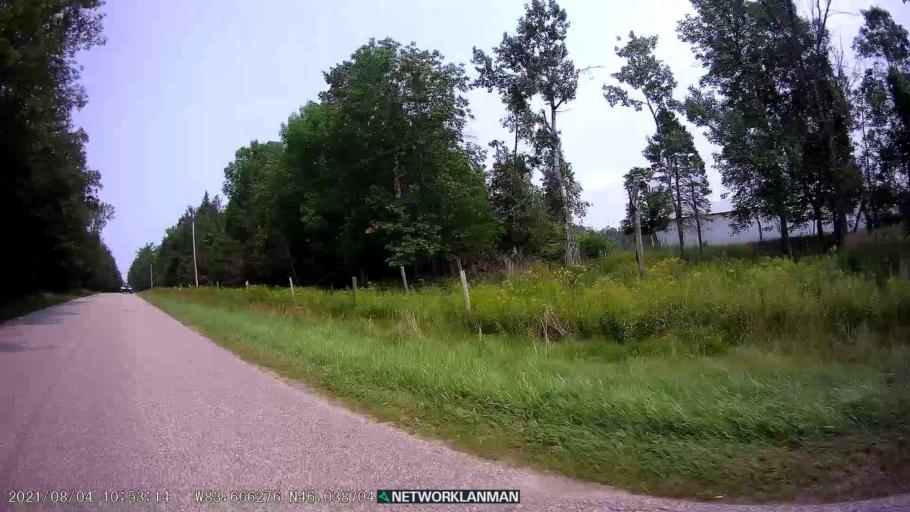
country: CA
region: Ontario
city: Thessalon
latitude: 46.0397
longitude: -83.6663
